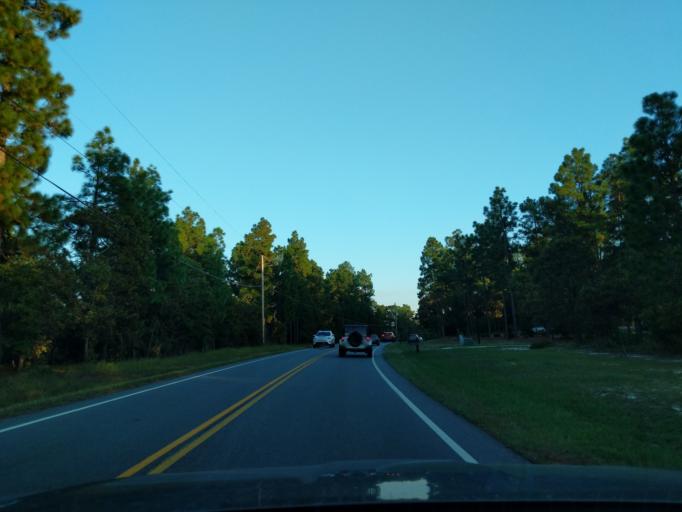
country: US
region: South Carolina
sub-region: Aiken County
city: Burnettown
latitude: 33.5360
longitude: -81.8628
